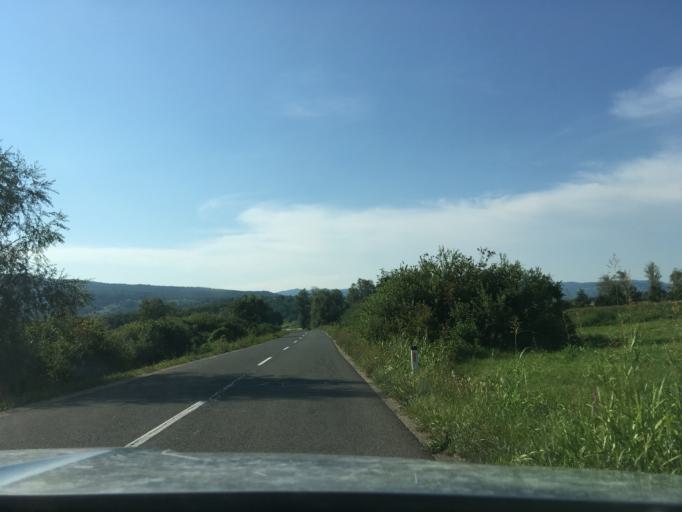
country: SI
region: Crnomelj
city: Crnomelj
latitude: 45.5218
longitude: 15.1686
